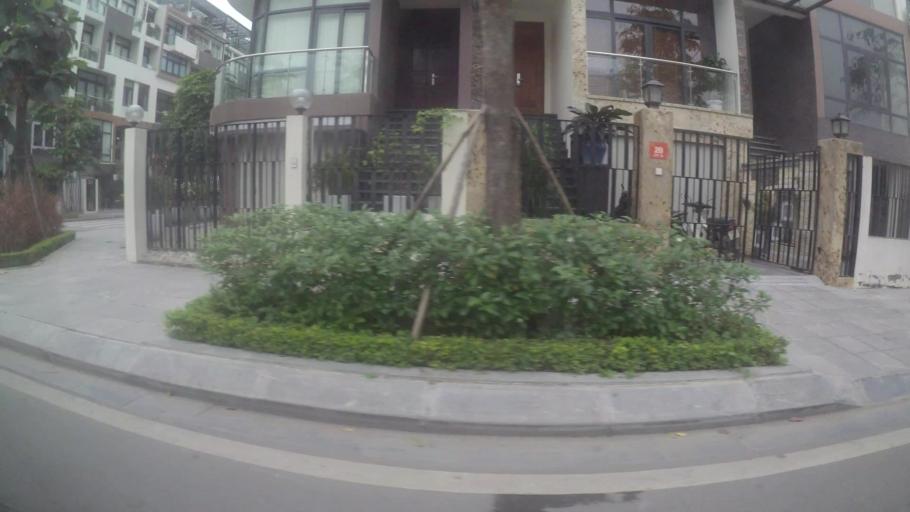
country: VN
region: Ha Noi
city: Cau Dien
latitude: 21.0348
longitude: 105.7680
